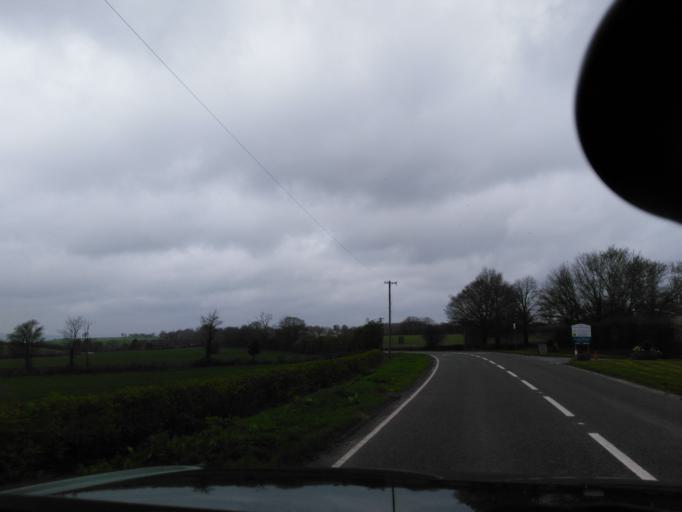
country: GB
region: England
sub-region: Somerset
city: Shepton Mallet
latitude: 51.1695
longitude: -2.5380
